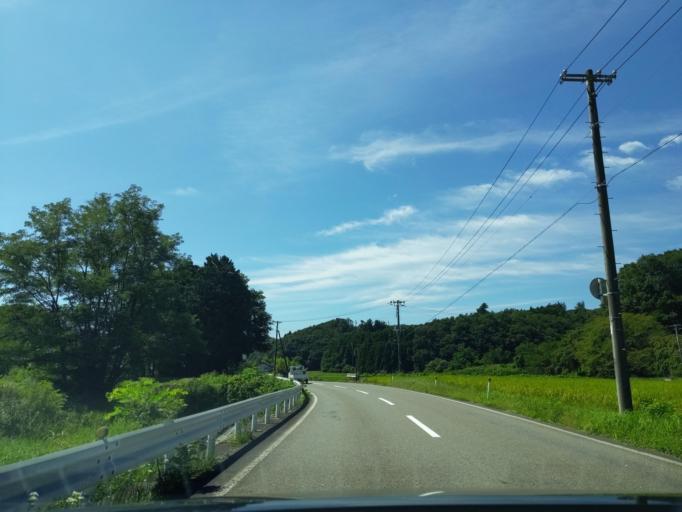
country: JP
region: Fukushima
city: Koriyama
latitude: 37.3860
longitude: 140.2607
